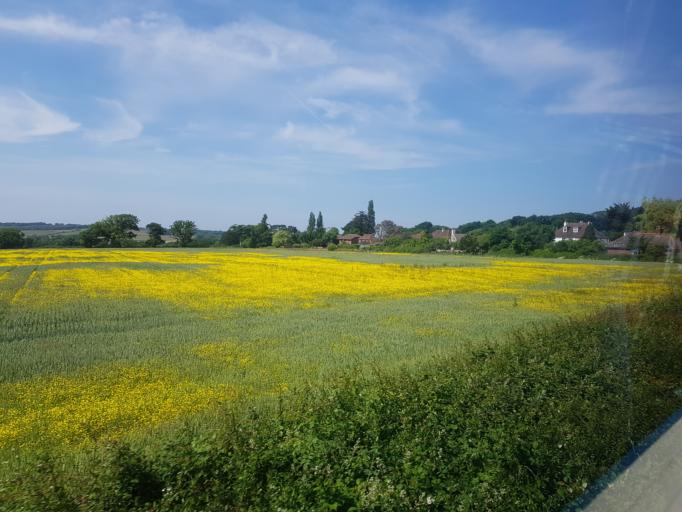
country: GB
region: England
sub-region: Isle of Wight
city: Newport
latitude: 50.7150
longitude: -1.2486
